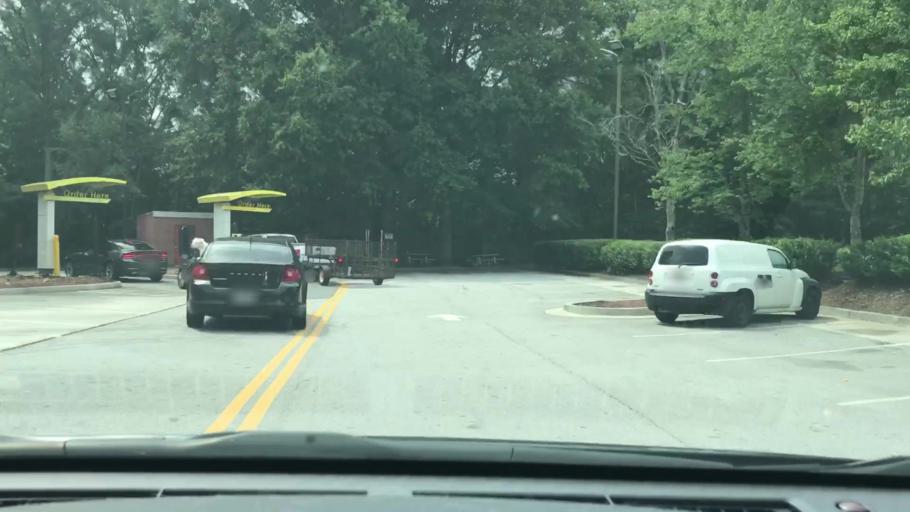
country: US
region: Georgia
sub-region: Rockdale County
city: Conyers
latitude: 33.6642
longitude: -84.0316
